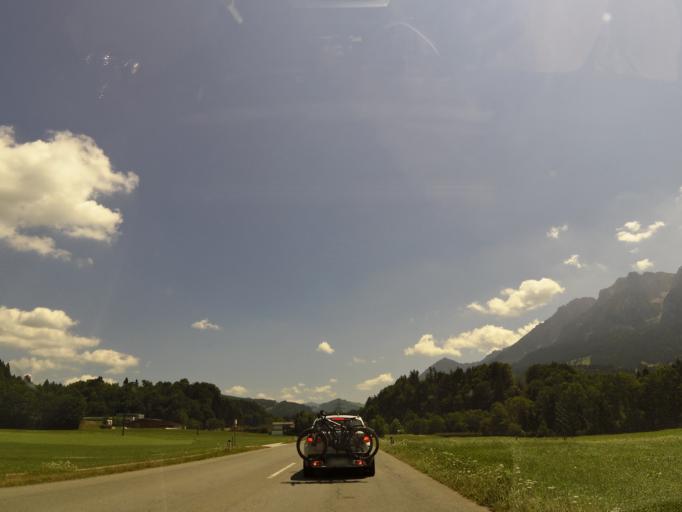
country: AT
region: Tyrol
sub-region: Politischer Bezirk Kufstein
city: Niederndorf
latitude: 47.6481
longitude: 12.2248
